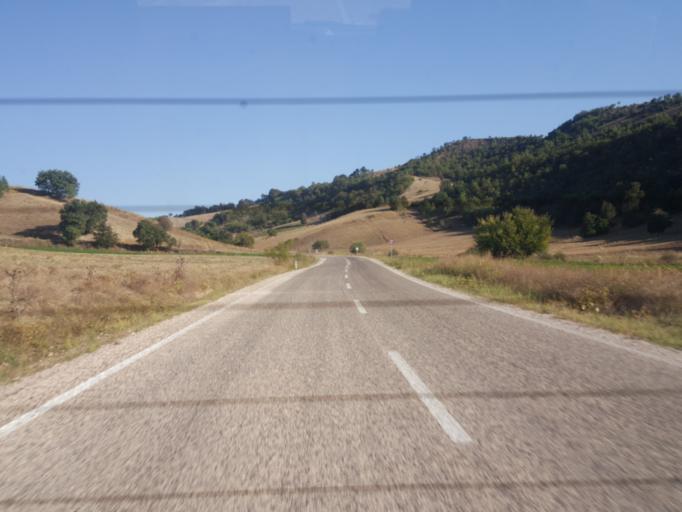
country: TR
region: Amasya
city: Tasova
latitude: 40.7204
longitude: 36.3036
